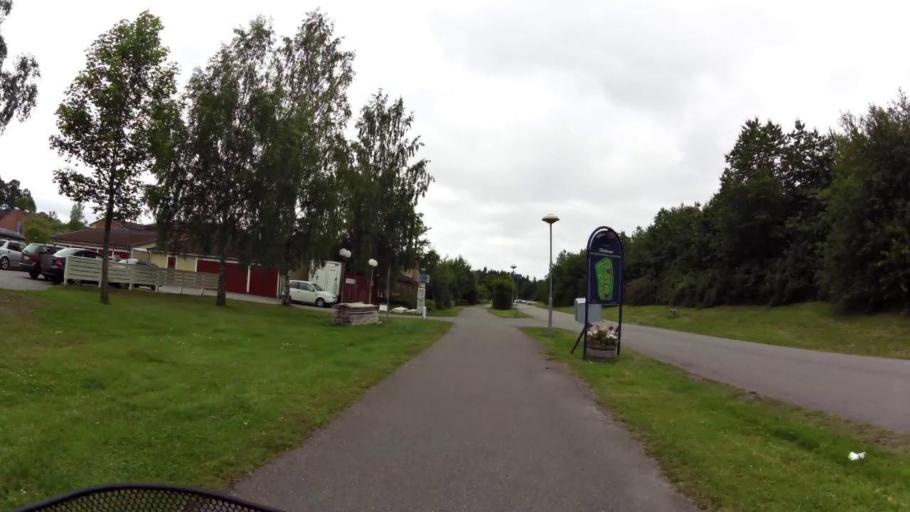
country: SE
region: OEstergoetland
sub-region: Linkopings Kommun
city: Sturefors
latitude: 58.3720
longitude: 15.6831
